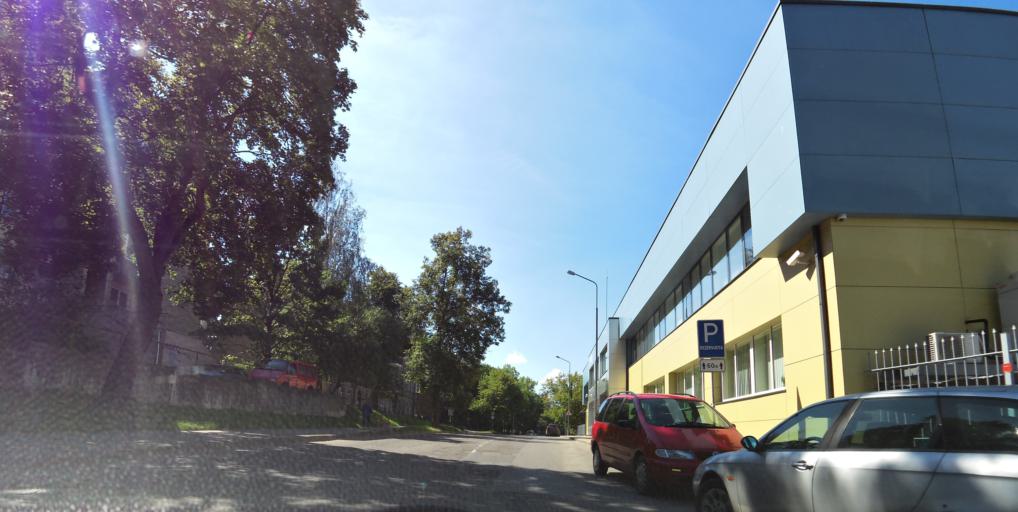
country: LT
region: Vilnius County
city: Naujamiestis
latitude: 54.6686
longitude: 25.2857
